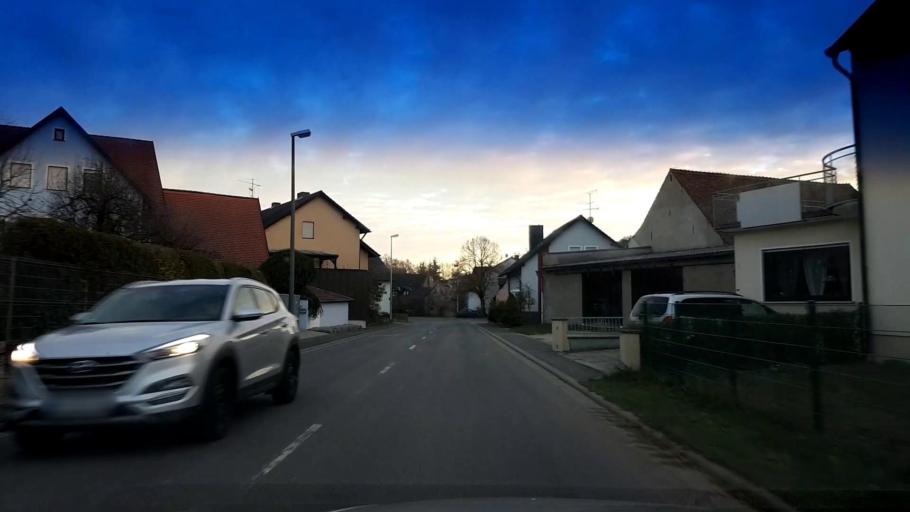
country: DE
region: Bavaria
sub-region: Upper Franconia
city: Walsdorf
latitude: 49.8829
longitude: 10.7586
